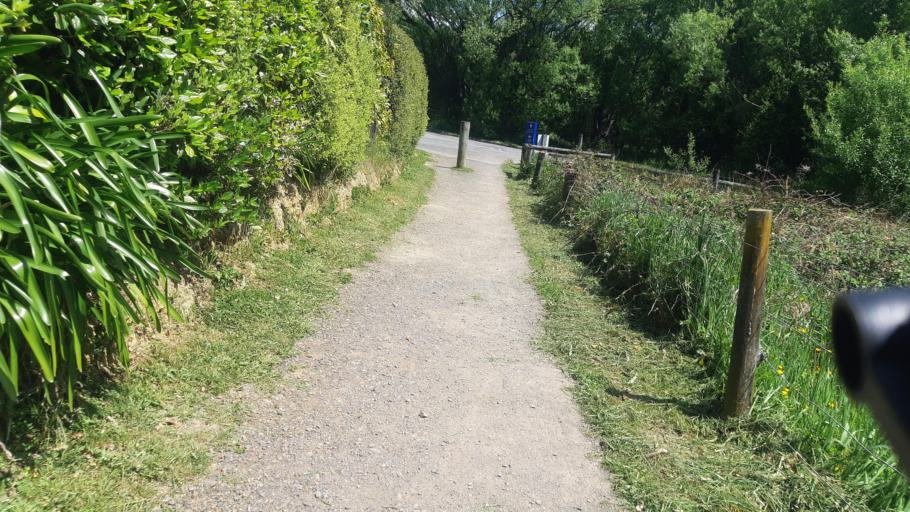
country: NZ
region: Marlborough
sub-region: Marlborough District
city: Picton
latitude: -41.2725
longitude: 174.0280
